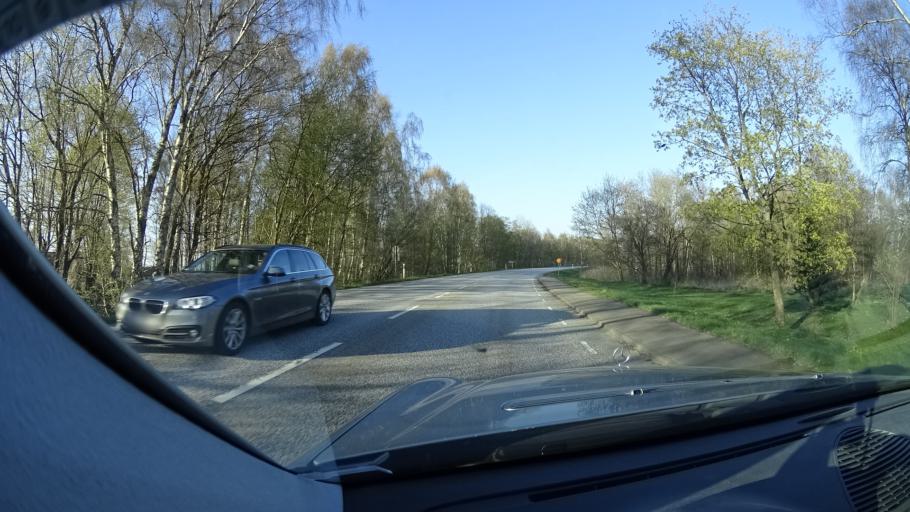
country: SE
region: Skane
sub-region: Hoors Kommun
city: Satofta
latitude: 55.8733
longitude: 13.4955
